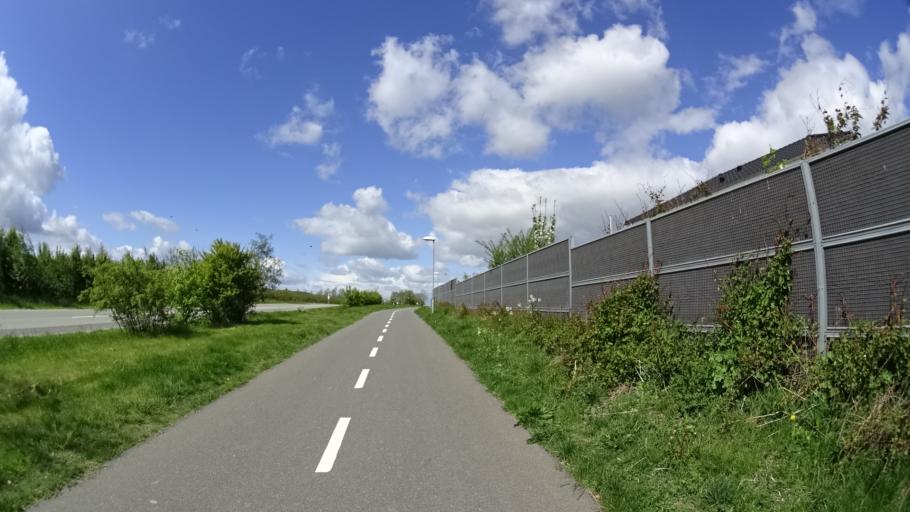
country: DK
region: Central Jutland
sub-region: Arhus Kommune
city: Stavtrup
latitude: 56.1291
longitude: 10.1049
